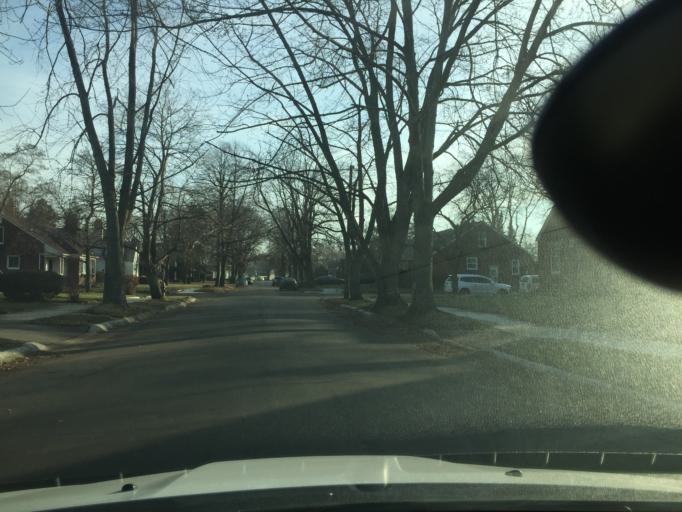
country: US
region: Michigan
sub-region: Wayne County
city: Harper Woods
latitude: 42.4339
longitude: -82.9563
